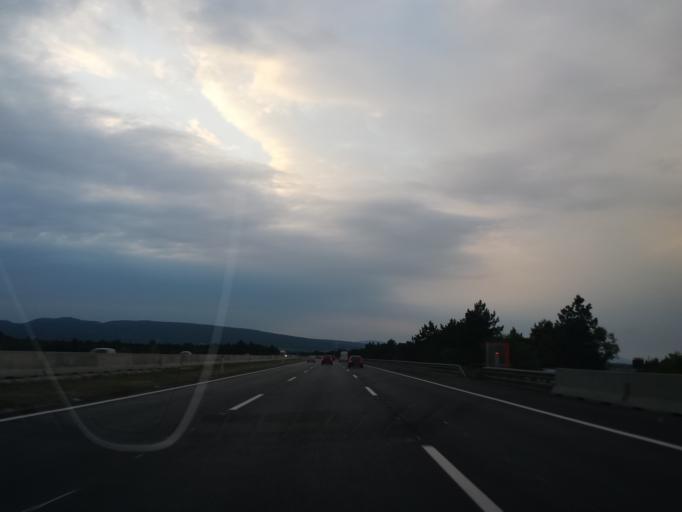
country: AT
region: Lower Austria
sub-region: Wiener Neustadt Stadt
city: Wiener Neustadt
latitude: 47.8024
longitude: 16.2008
